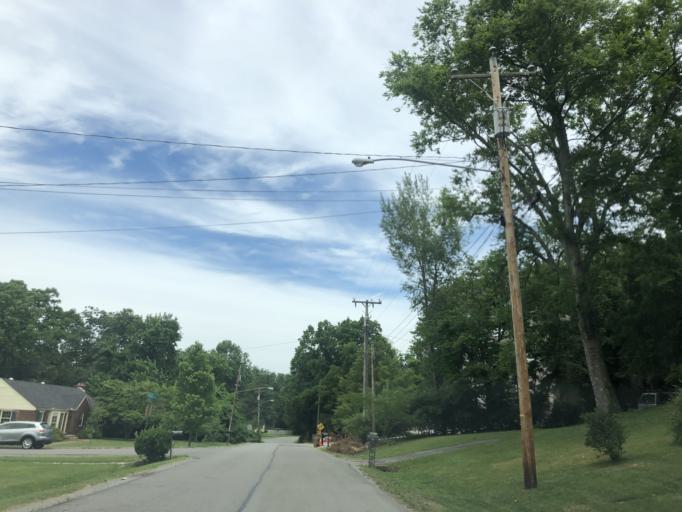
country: US
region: Tennessee
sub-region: Davidson County
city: Oak Hill
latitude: 36.1072
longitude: -86.7851
